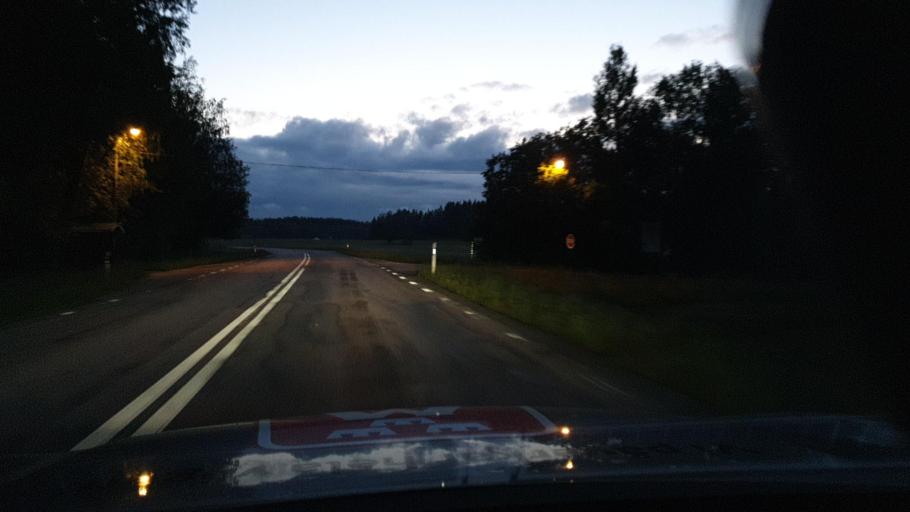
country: SE
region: OErebro
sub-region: Karlskoga Kommun
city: Karlskoga
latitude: 59.3899
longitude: 14.4700
